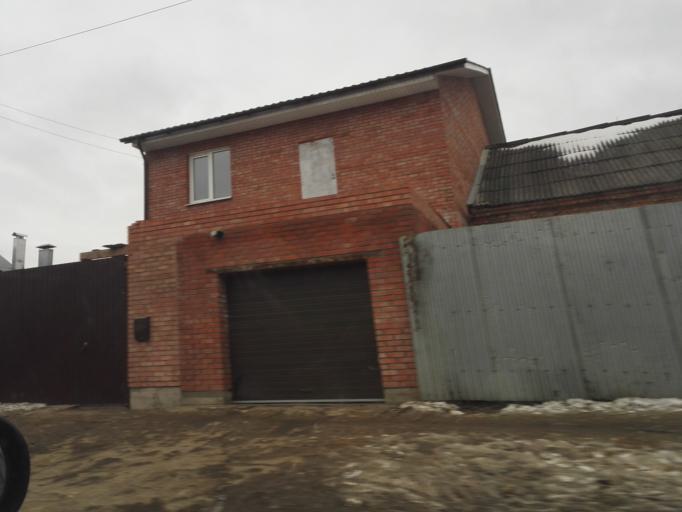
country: RU
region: Tula
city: Tula
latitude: 54.1713
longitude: 37.6033
